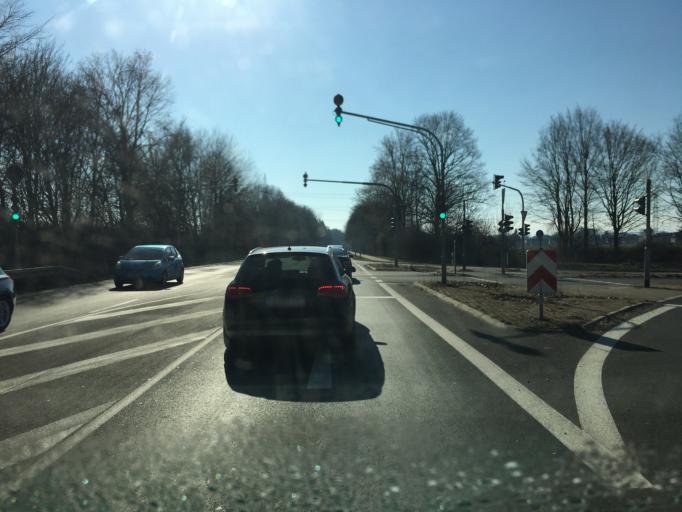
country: DE
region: North Rhine-Westphalia
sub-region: Regierungsbezirk Koln
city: Pulheim
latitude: 50.9700
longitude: 6.7947
